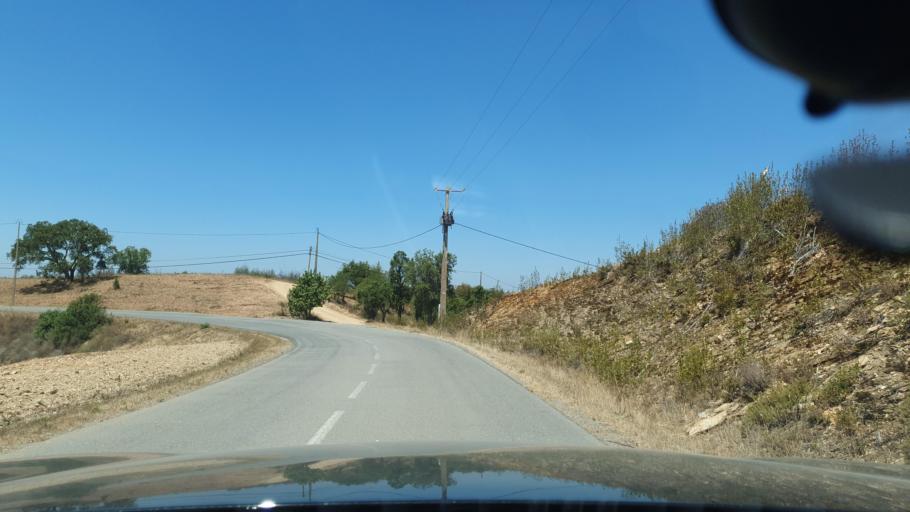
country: PT
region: Beja
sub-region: Odemira
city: Odemira
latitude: 37.5521
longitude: -8.4388
